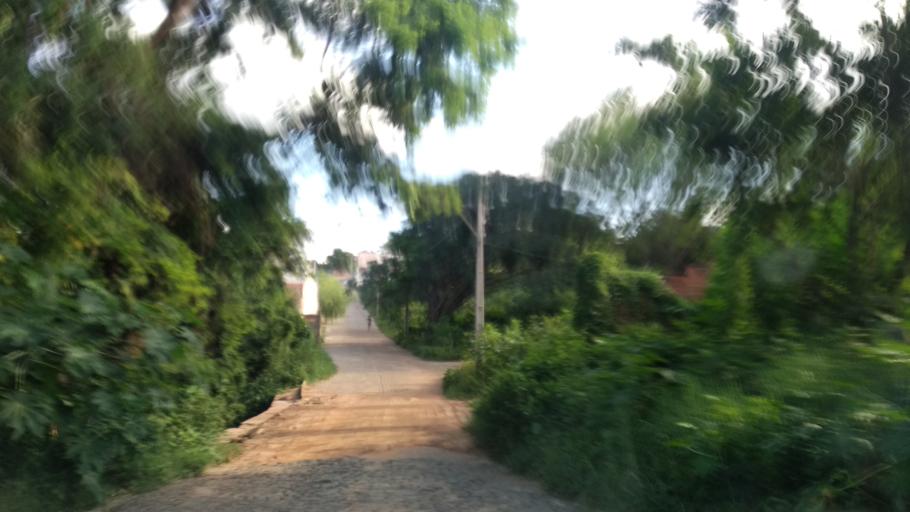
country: BR
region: Bahia
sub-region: Caetite
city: Caetite
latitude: -14.0726
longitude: -42.4845
